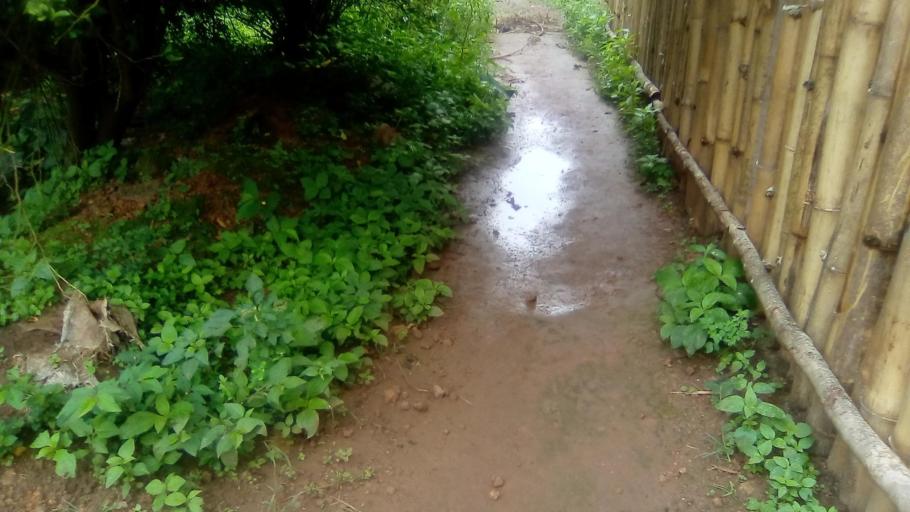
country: SL
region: Southern Province
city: Moyamba
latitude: 8.1594
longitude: -12.4289
